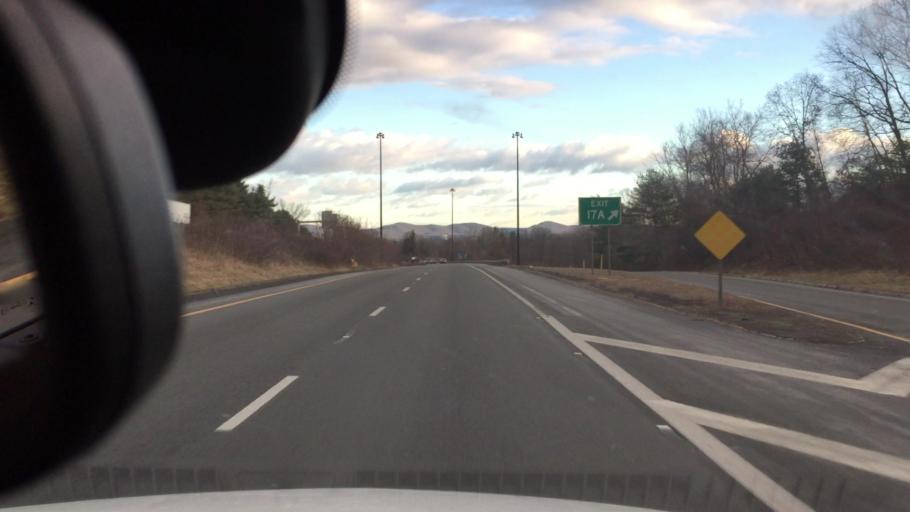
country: US
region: Massachusetts
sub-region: Hampden County
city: Holyoke
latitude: 42.2083
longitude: -72.6364
